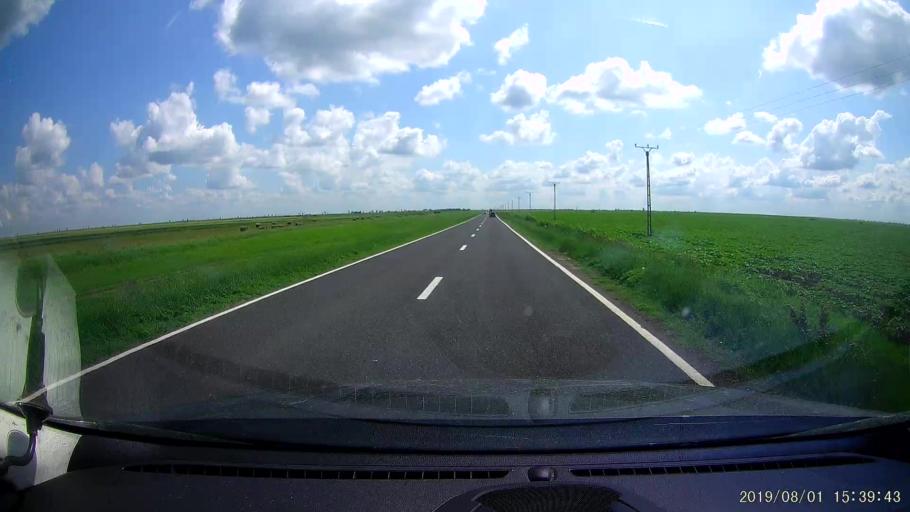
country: RO
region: Braila
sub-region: Comuna Baraganul
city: Baraganul
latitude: 44.8513
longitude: 27.5543
